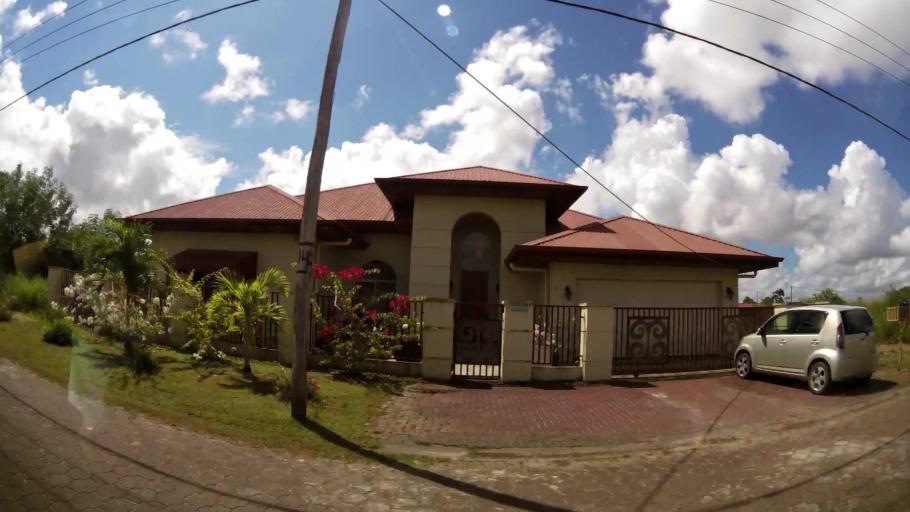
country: SR
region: Paramaribo
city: Paramaribo
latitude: 5.8669
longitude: -55.1302
